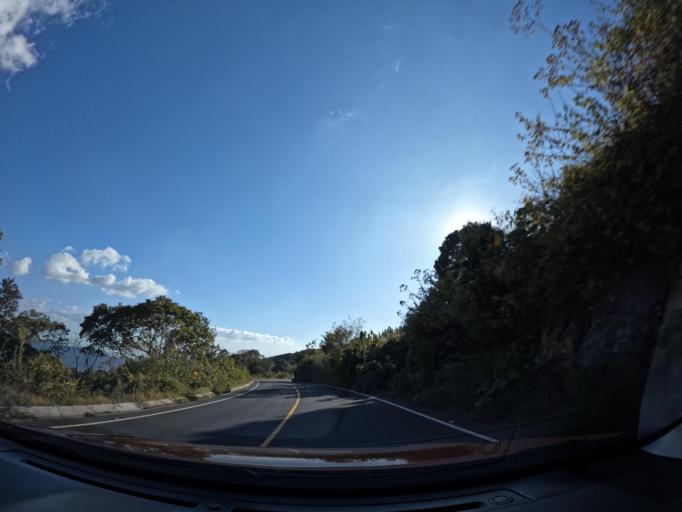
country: GT
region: Sacatepequez
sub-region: Municipio de Santa Maria de Jesus
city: Santa Maria de Jesus
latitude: 14.4690
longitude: -90.6930
